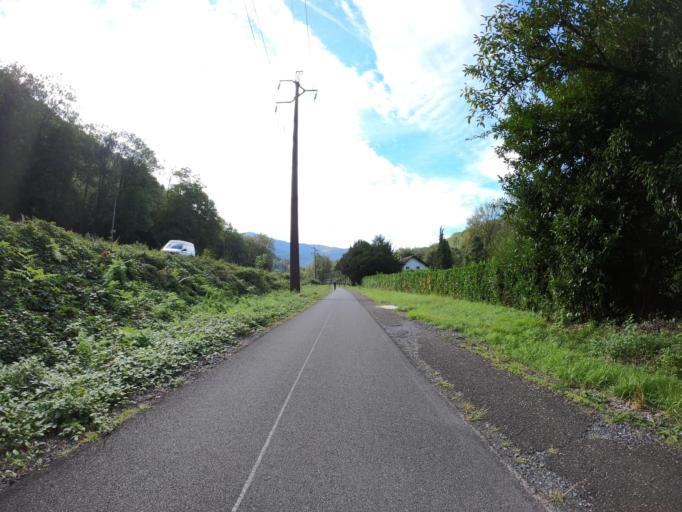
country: FR
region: Midi-Pyrenees
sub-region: Departement des Hautes-Pyrenees
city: Lourdes
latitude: 43.0772
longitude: -0.0412
